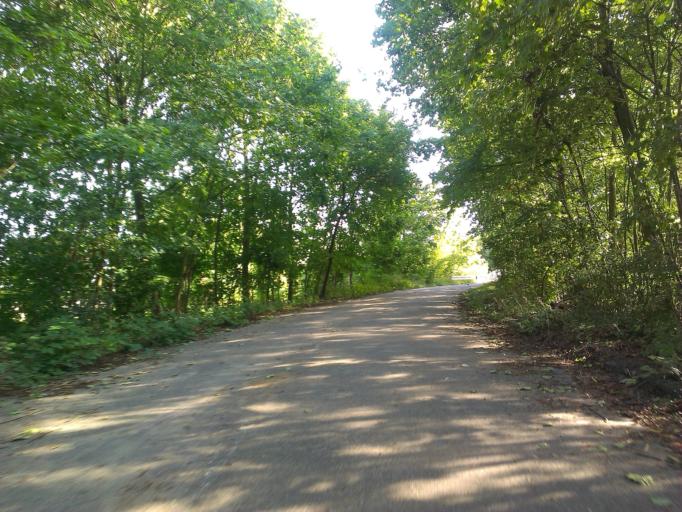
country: DE
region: Baden-Wuerttemberg
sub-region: Karlsruhe Region
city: Ilvesheim
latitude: 49.4434
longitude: 8.5604
